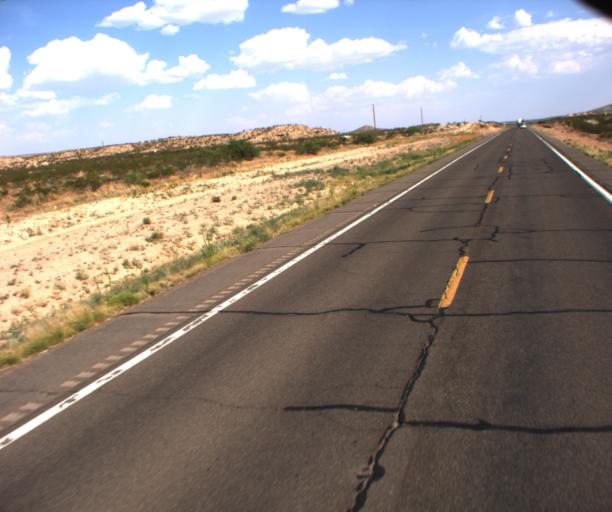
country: US
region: Arizona
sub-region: Greenlee County
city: Clifton
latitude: 32.7806
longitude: -109.1576
